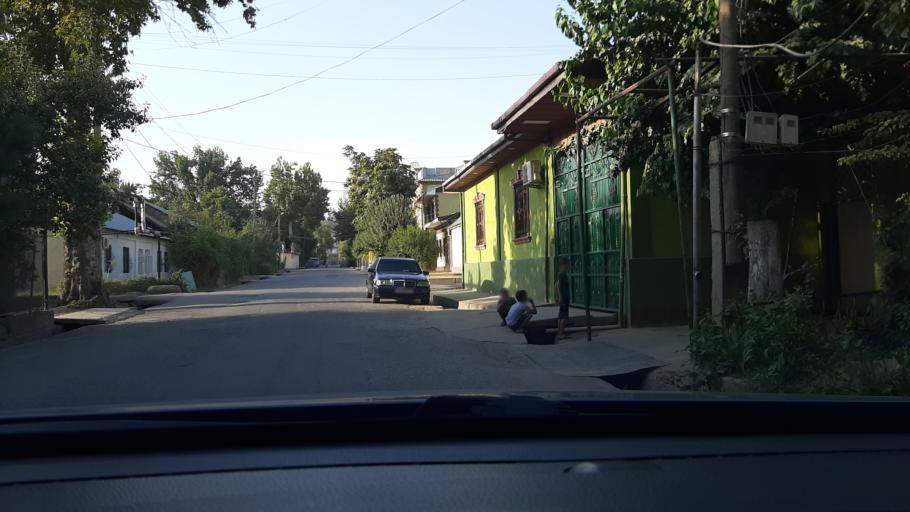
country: TJ
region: Dushanbe
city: Dushanbe
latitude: 38.5639
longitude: 68.8118
